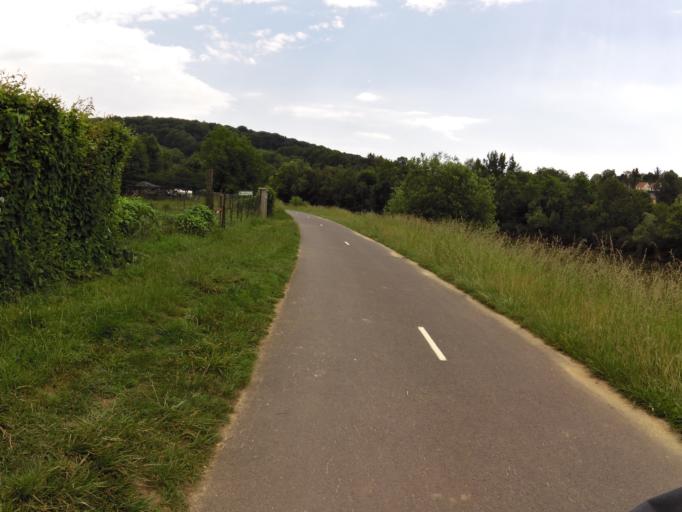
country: FR
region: Champagne-Ardenne
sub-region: Departement des Ardennes
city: Montcy-Notre-Dame
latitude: 49.7714
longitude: 4.7426
